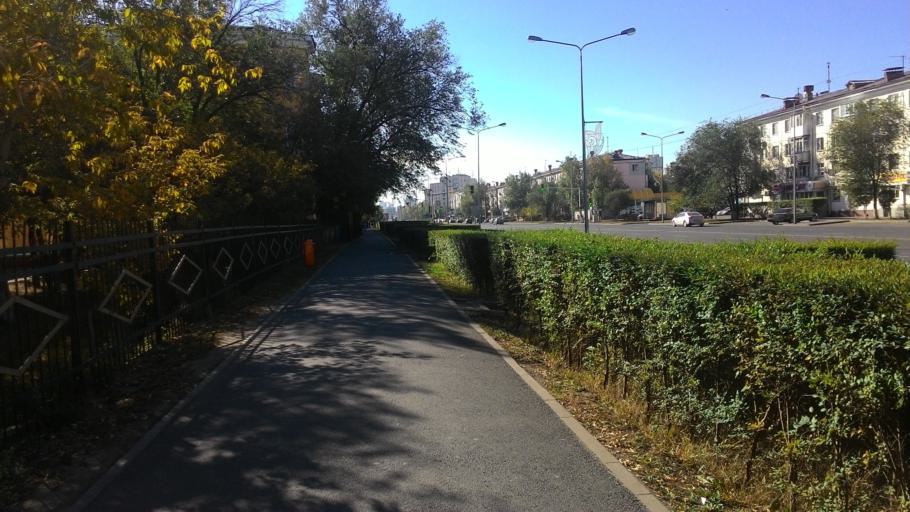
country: KZ
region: Astana Qalasy
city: Astana
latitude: 51.1845
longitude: 71.4089
